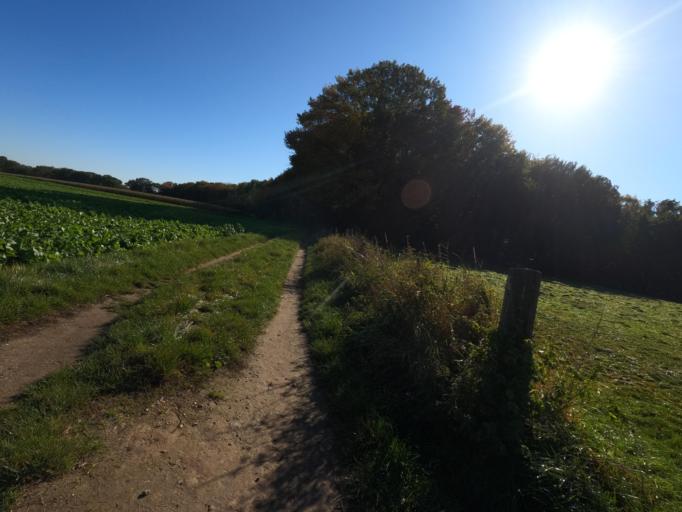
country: DE
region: North Rhine-Westphalia
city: Huckelhoven
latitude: 51.0567
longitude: 6.2401
